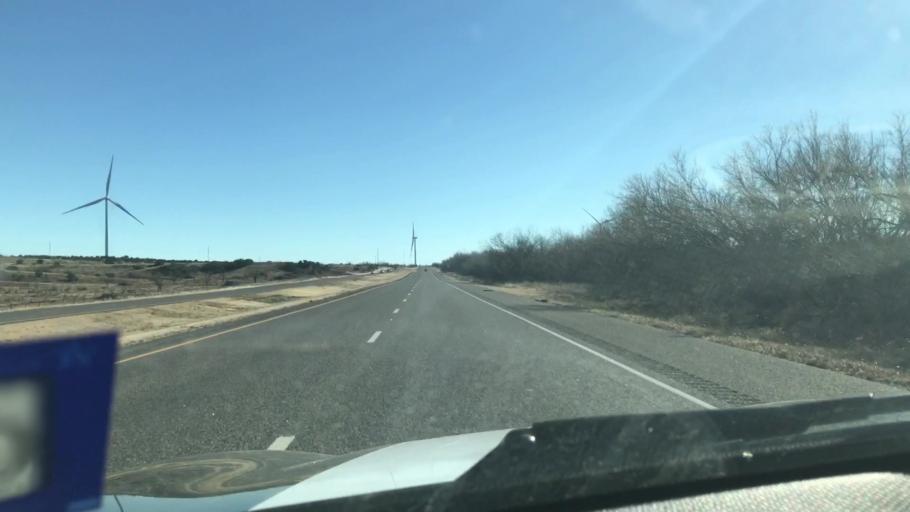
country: US
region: Texas
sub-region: Scurry County
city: Snyder
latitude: 32.8958
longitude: -101.0553
